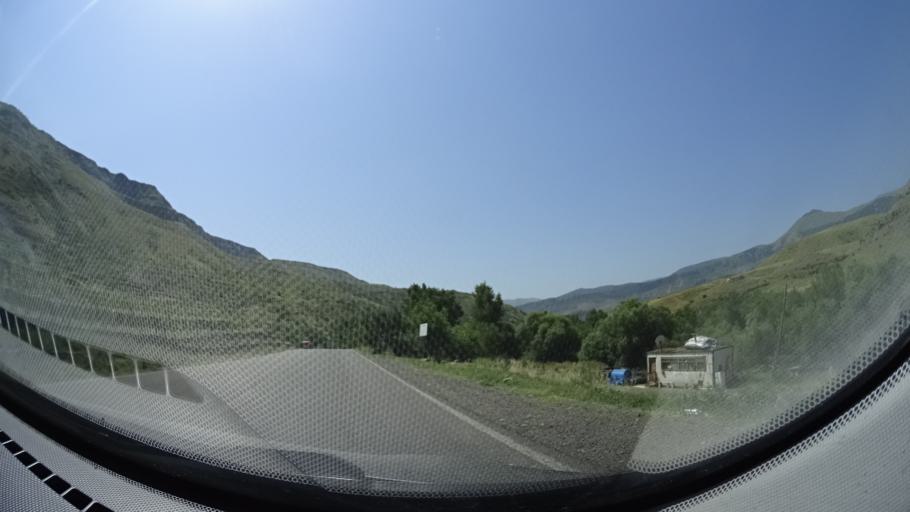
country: GE
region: Samtskhe-Javakheti
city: Aspindza
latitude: 41.5345
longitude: 43.2601
